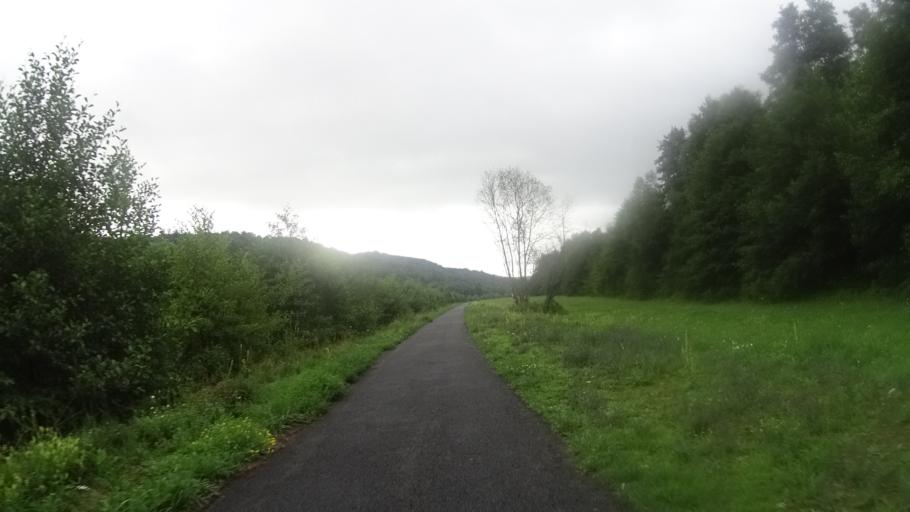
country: FR
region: Lorraine
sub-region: Departement de Meurthe-et-Moselle
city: Chaligny
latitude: 48.6506
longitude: 6.0376
